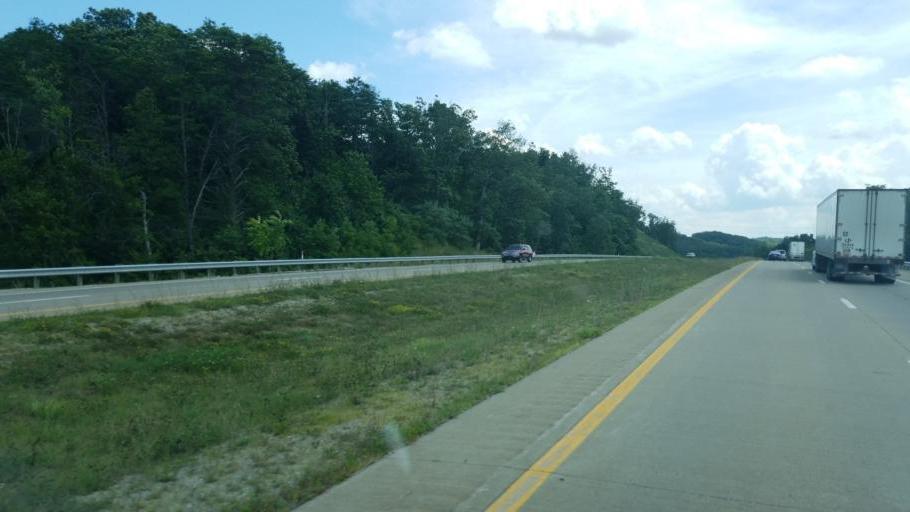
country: US
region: West Virginia
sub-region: Mason County
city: Point Pleasant
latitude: 38.7747
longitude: -82.0578
